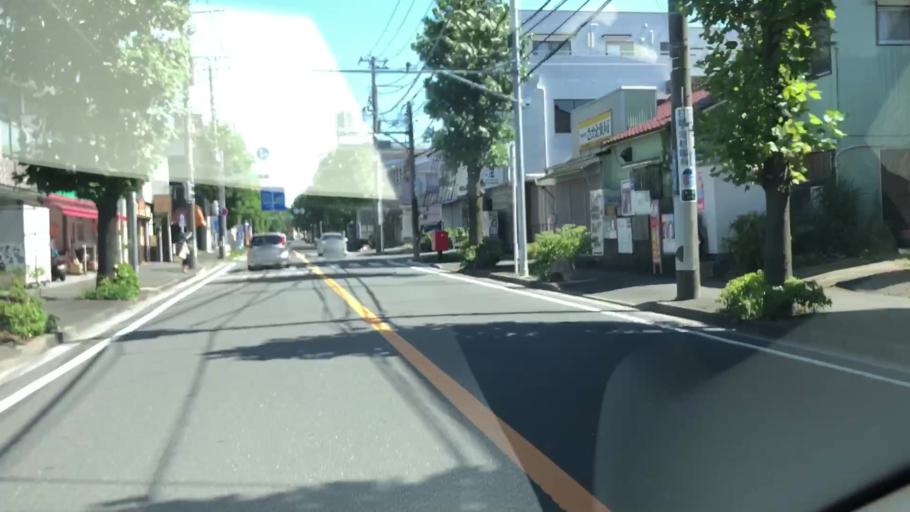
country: JP
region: Kanagawa
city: Yokohama
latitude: 35.3826
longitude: 139.6054
